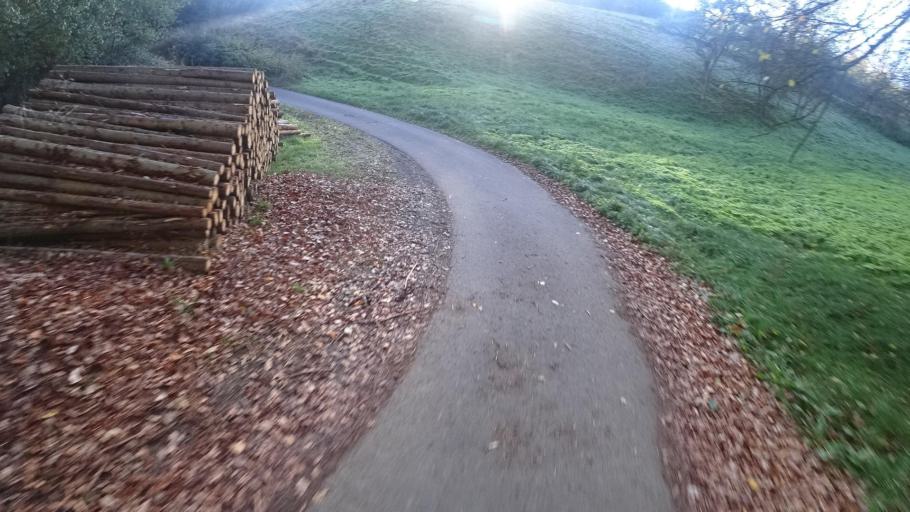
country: DE
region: Rheinland-Pfalz
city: Berg
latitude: 50.5283
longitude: 6.9351
